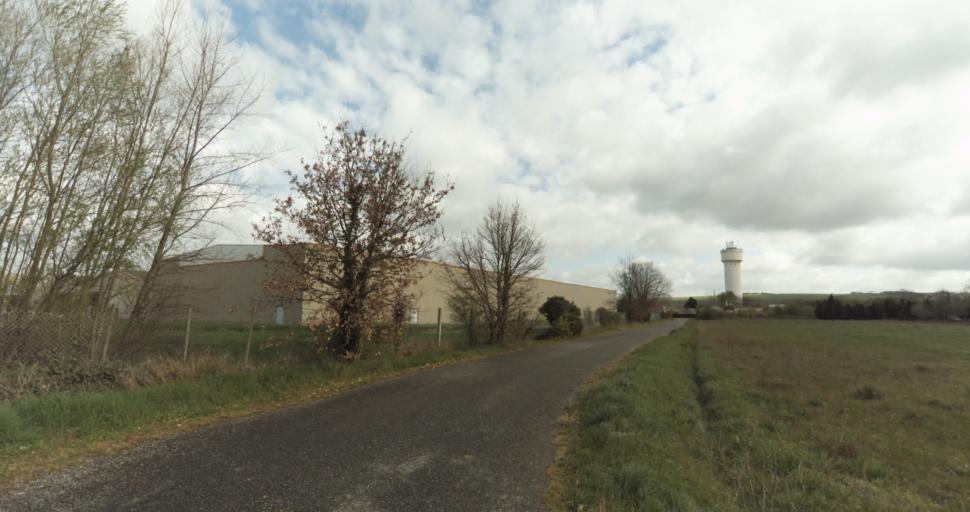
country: FR
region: Midi-Pyrenees
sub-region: Departement de la Haute-Garonne
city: Auterive
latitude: 43.3581
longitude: 1.4607
